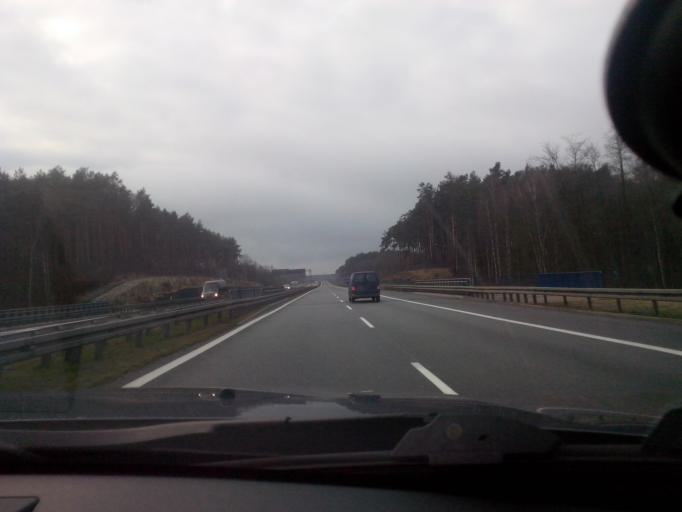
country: PL
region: Lubusz
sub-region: Powiat slubicki
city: Rzepin
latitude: 52.3329
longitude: 14.8728
